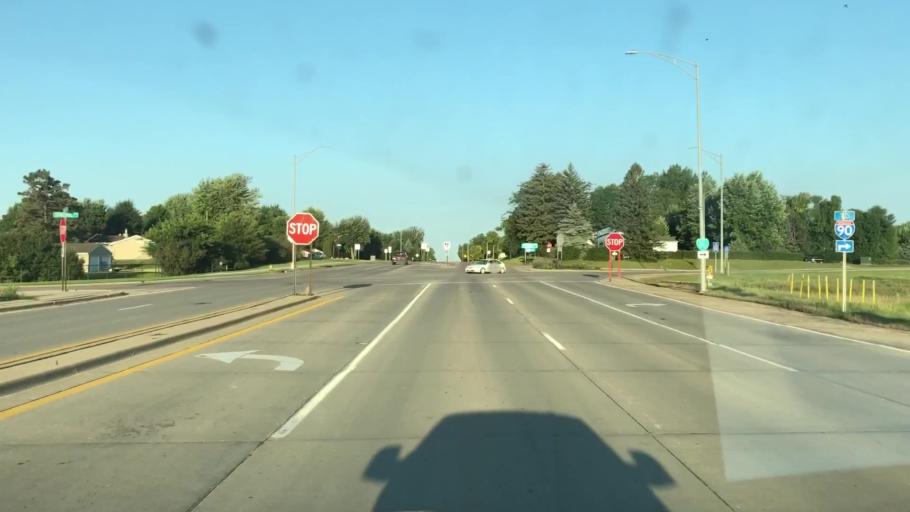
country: US
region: Minnesota
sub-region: Nobles County
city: Worthington
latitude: 43.6311
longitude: -95.6126
